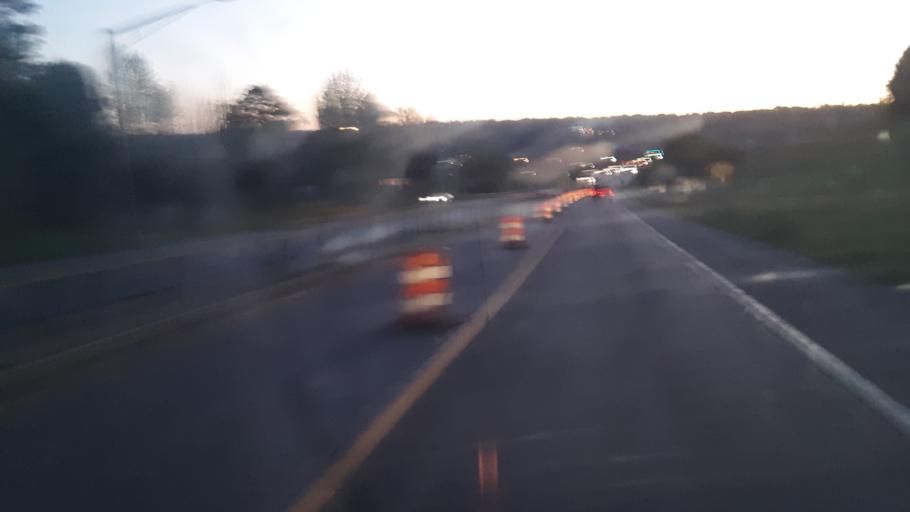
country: US
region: New York
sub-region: Montgomery County
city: Amsterdam
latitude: 42.9310
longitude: -74.1964
